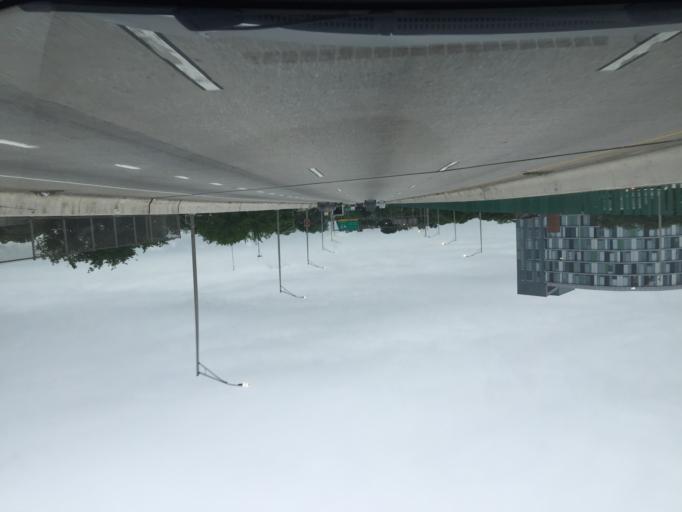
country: US
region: Maryland
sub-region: City of Baltimore
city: Baltimore
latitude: 39.3100
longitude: -76.6214
